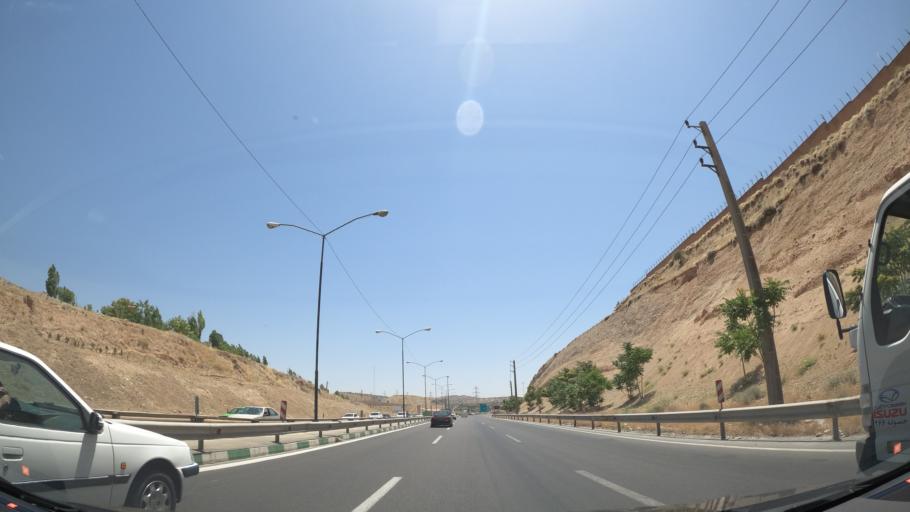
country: IR
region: Tehran
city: Tehran
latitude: 35.7409
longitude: 51.6213
